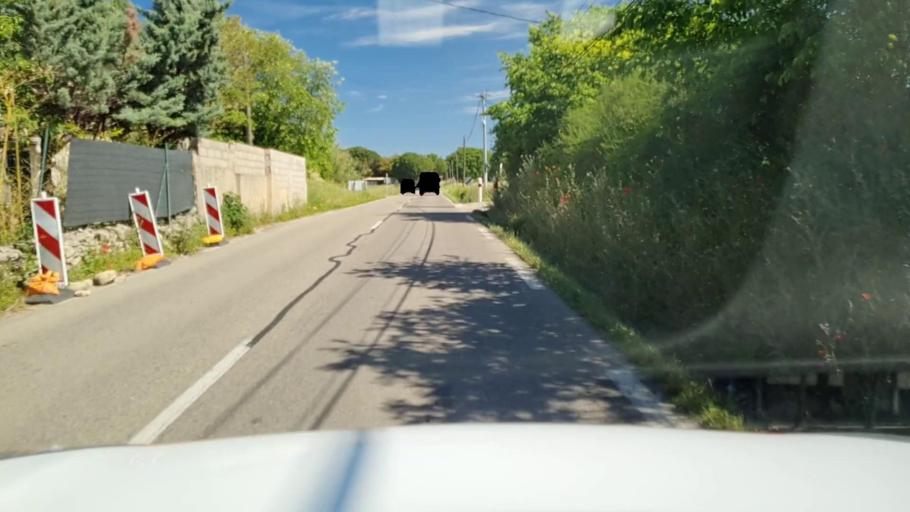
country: FR
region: Languedoc-Roussillon
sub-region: Departement du Gard
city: Sommieres
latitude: 43.7987
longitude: 4.0861
